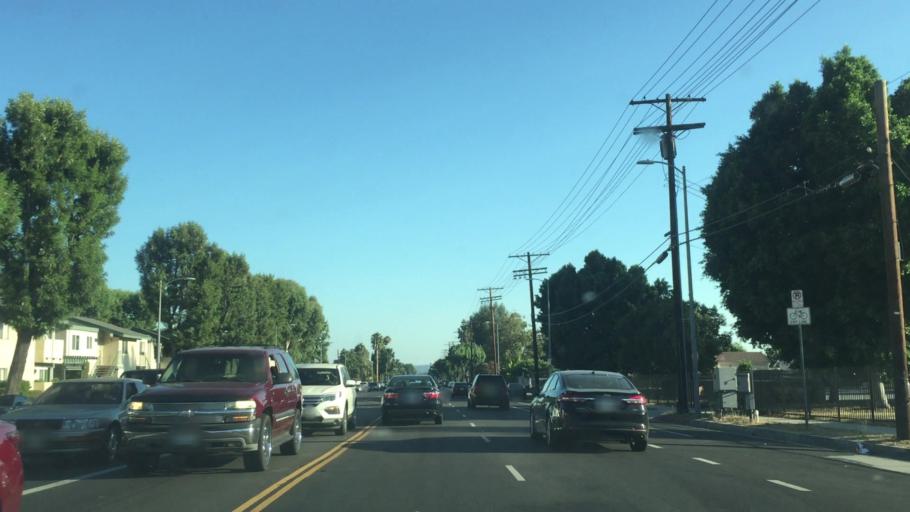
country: US
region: California
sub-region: Los Angeles County
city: San Fernando
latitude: 34.2644
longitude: -118.4849
